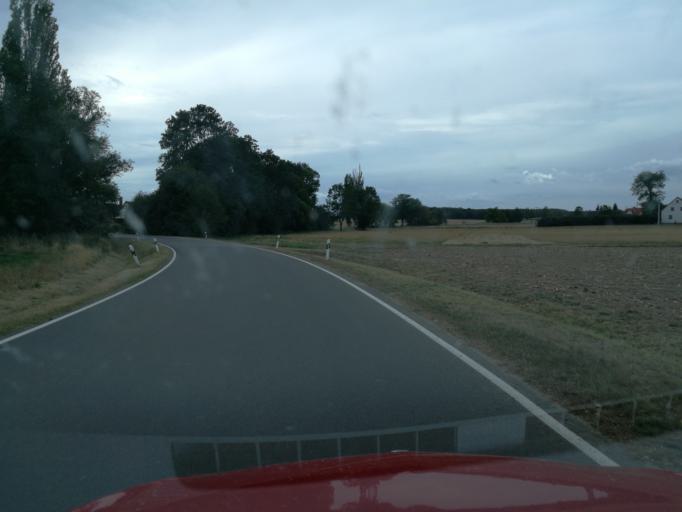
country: DE
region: Saxony
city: Mugeln
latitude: 51.2673
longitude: 13.0624
